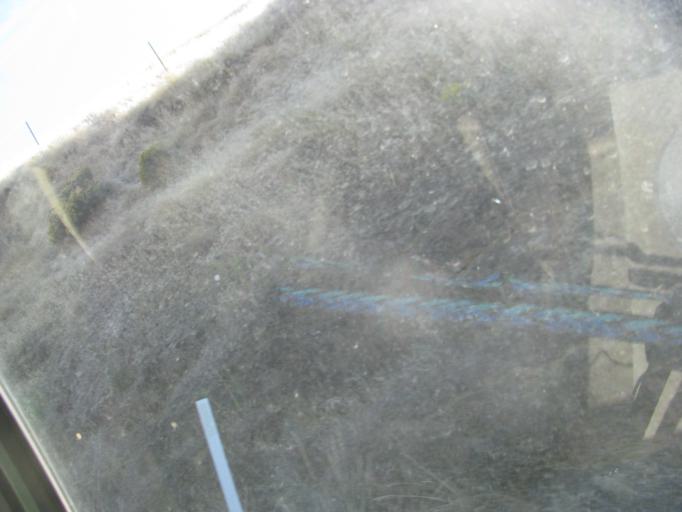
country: US
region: Washington
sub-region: Asotin County
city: Asotin
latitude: 46.3212
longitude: -117.0476
